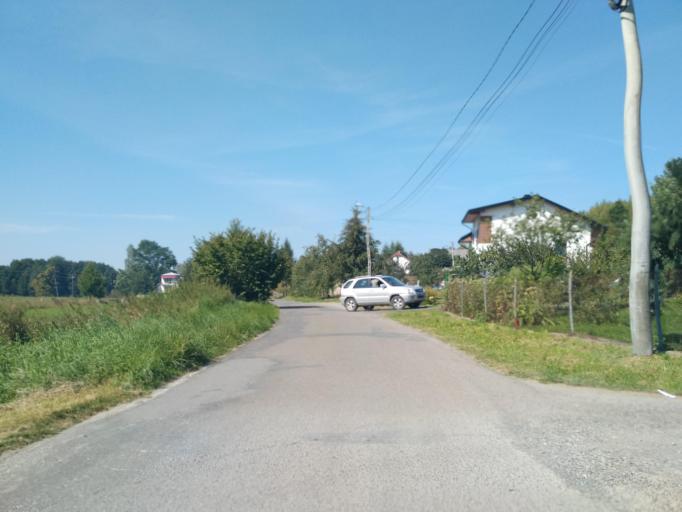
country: PL
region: Subcarpathian Voivodeship
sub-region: Powiat brzozowski
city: Grabownica Starzenska
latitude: 49.6470
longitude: 22.0961
